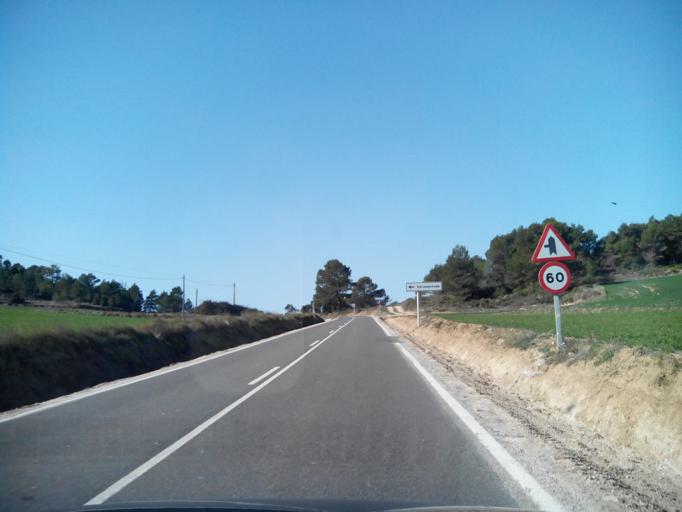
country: ES
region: Catalonia
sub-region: Provincia de Tarragona
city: Conesa
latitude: 41.4945
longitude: 1.3221
